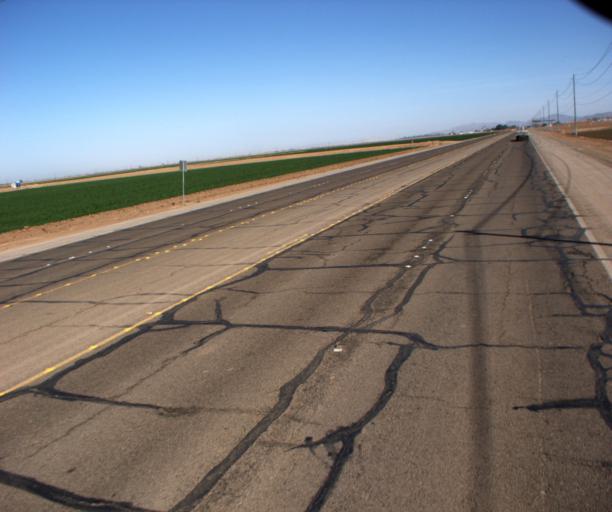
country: US
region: Arizona
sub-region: Yuma County
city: Somerton
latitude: 32.5726
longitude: -114.7698
